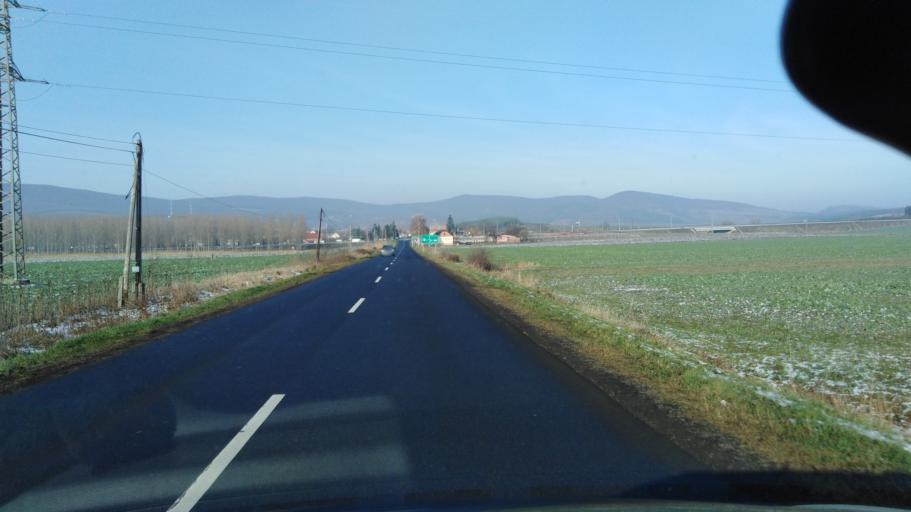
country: HU
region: Nograd
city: Paszto
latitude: 47.9414
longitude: 19.7056
